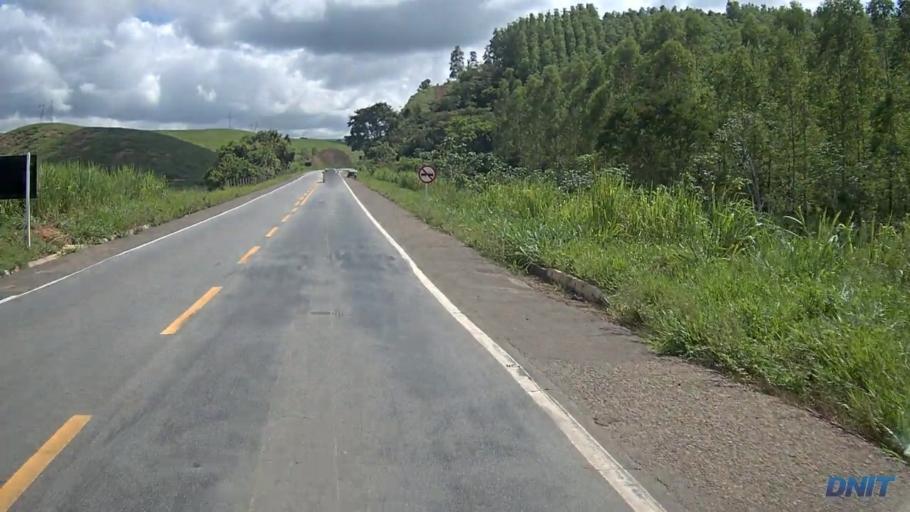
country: BR
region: Minas Gerais
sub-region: Belo Oriente
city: Belo Oriente
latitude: -19.1095
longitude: -42.2028
